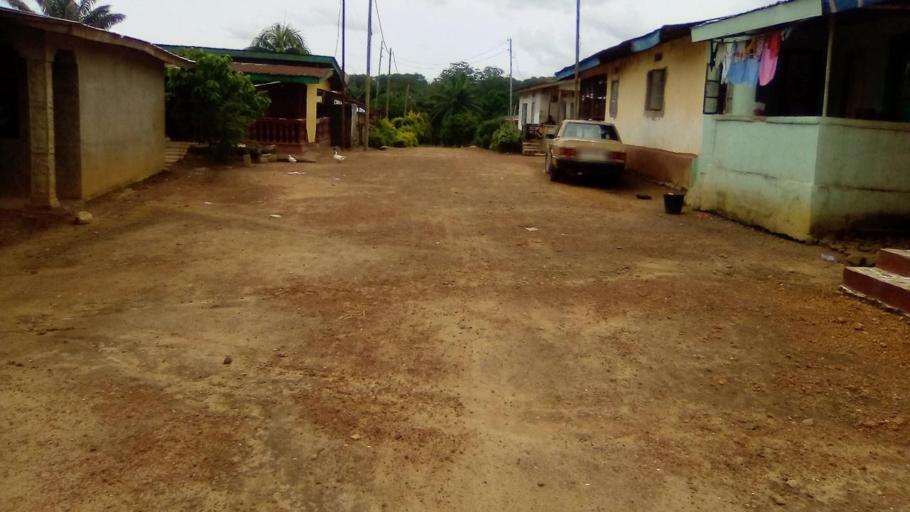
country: SL
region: Southern Province
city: Bo
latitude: 7.9505
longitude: -11.7517
